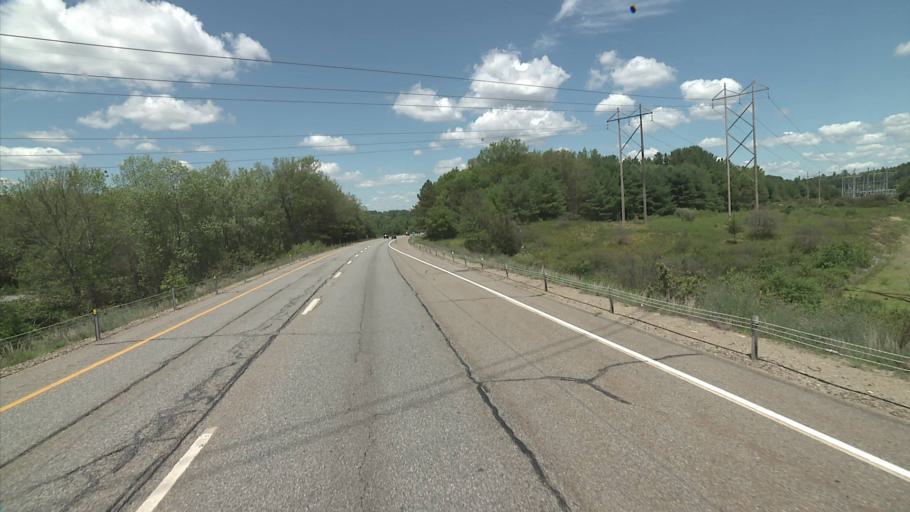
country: US
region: Connecticut
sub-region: Windham County
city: Putnam
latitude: 41.8780
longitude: -71.8948
